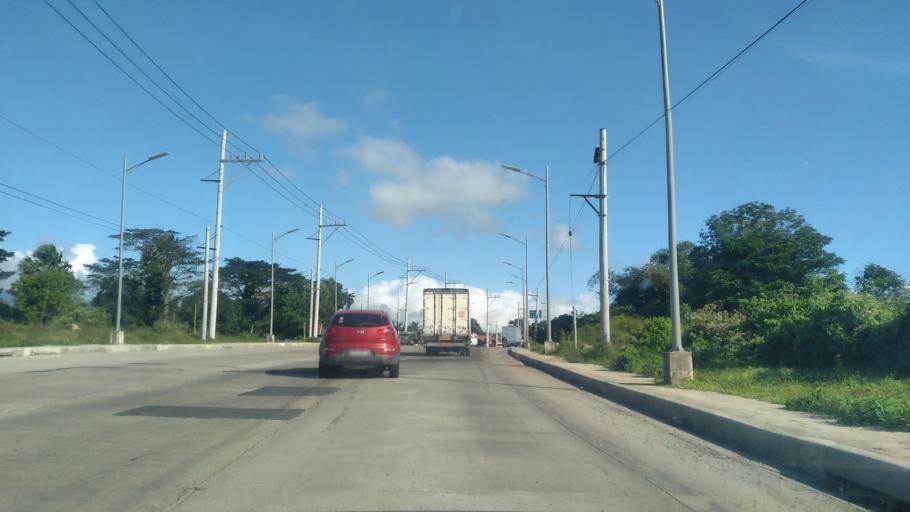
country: PH
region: Calabarzon
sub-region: Province of Quezon
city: Isabang
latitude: 13.9497
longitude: 121.5771
